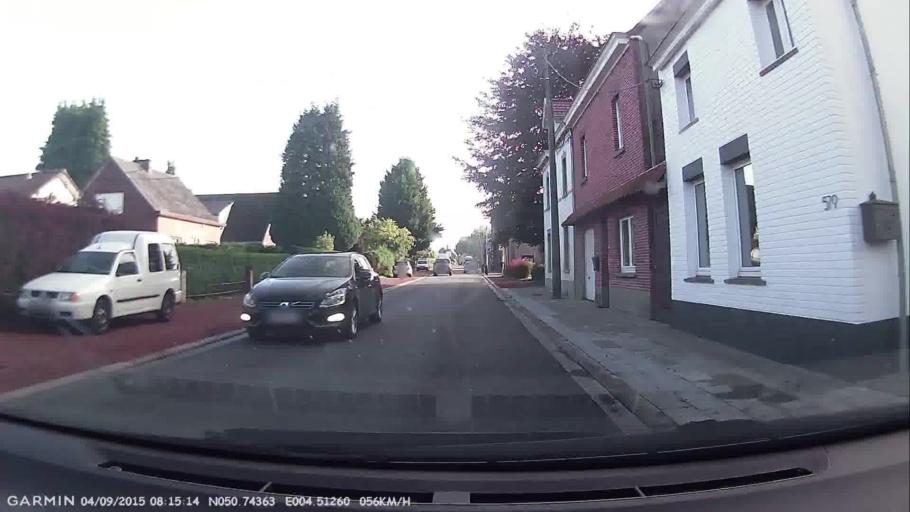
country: BE
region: Wallonia
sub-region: Province du Brabant Wallon
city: La Hulpe
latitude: 50.7438
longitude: 4.5129
